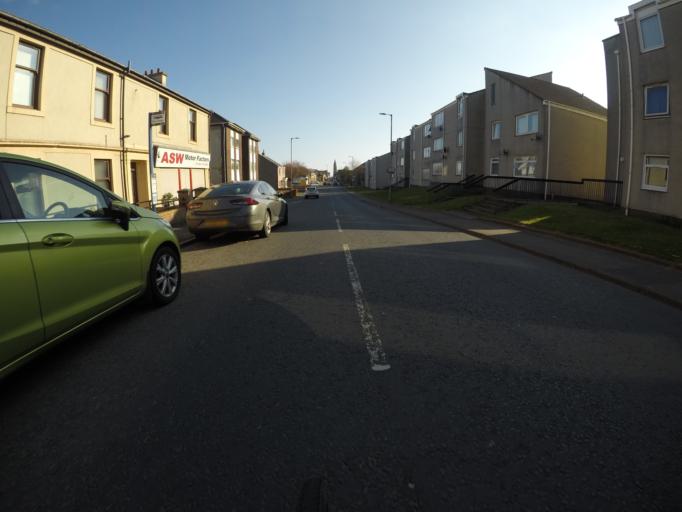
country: GB
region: Scotland
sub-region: North Ayrshire
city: Saltcoats
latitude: 55.6363
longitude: -4.7835
